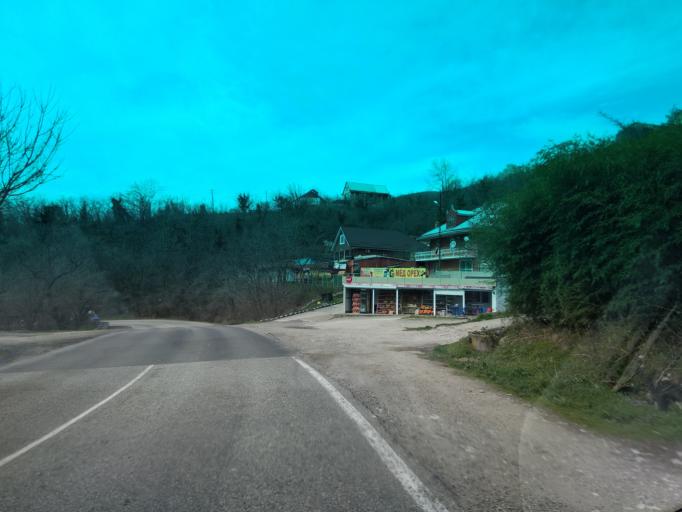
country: RU
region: Krasnodarskiy
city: Tuapse
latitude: 44.0896
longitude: 39.1230
